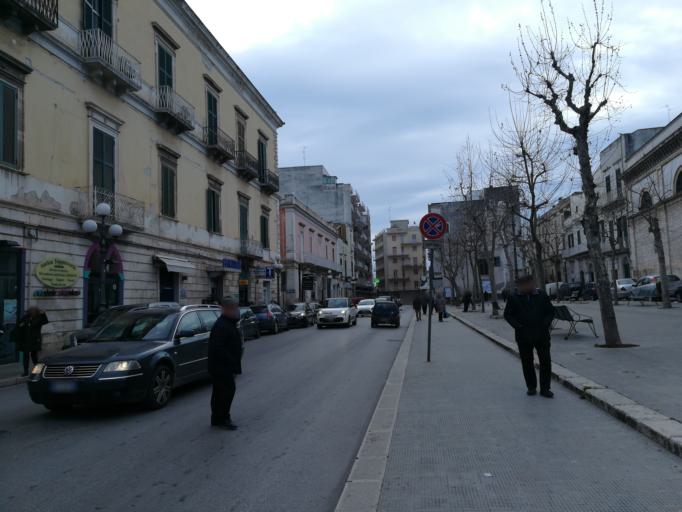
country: IT
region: Apulia
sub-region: Provincia di Bari
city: Bitonto
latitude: 41.1093
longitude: 16.6895
